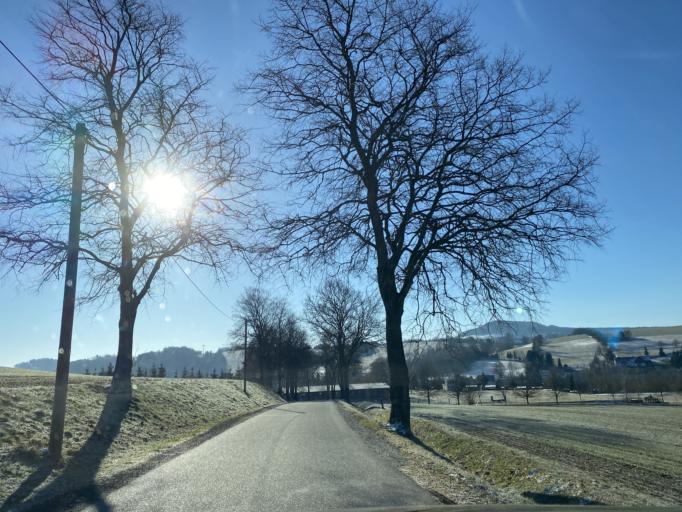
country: DE
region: Saxony
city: Wiesa
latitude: 50.6147
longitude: 13.0118
